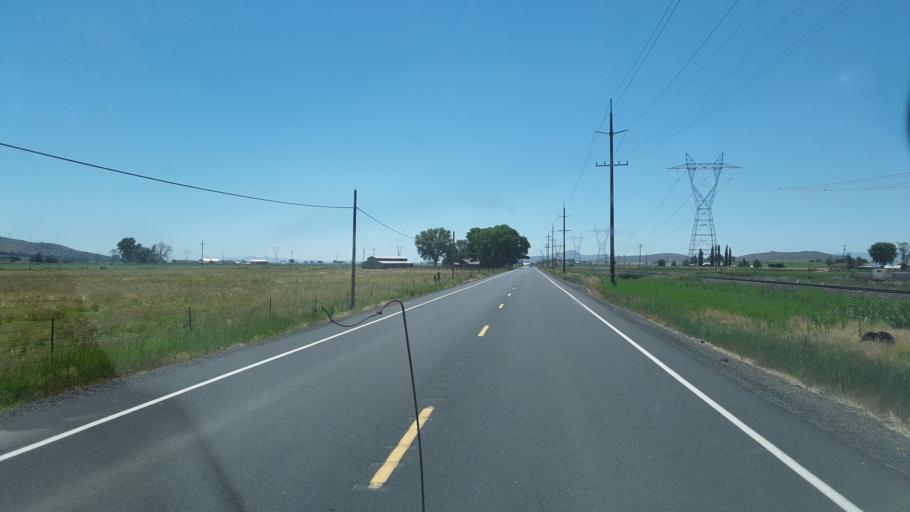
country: US
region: Oregon
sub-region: Klamath County
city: Altamont
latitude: 42.0862
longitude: -121.6825
